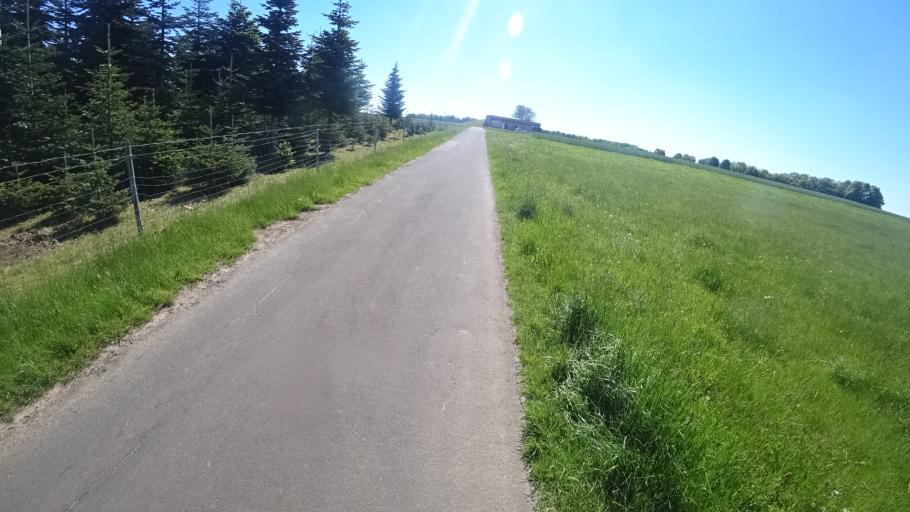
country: DE
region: Rheinland-Pfalz
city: Elkenroth
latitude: 50.7221
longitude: 7.8980
